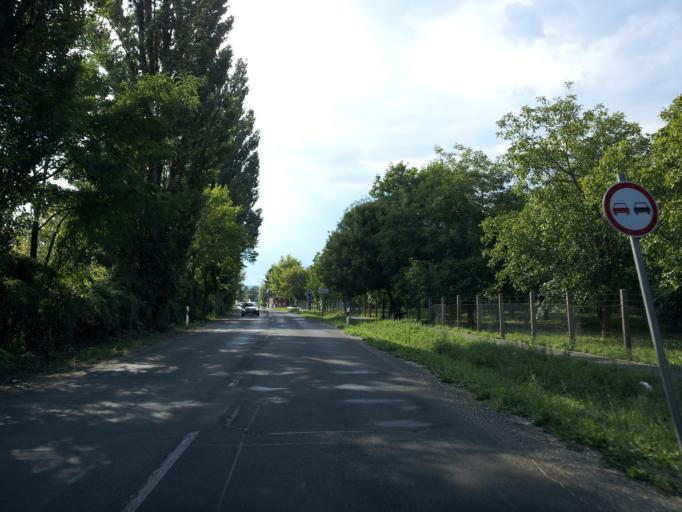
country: HU
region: Pest
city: Veroce
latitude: 47.8201
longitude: 19.0451
